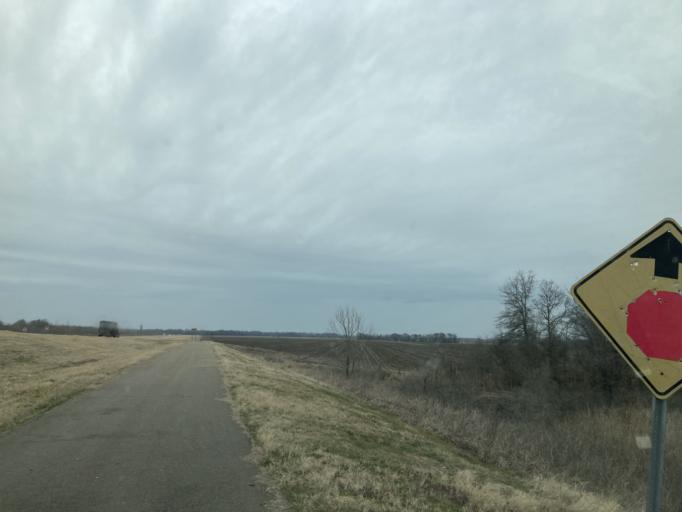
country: US
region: Mississippi
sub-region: Humphreys County
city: Belzoni
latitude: 33.0555
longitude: -90.4688
